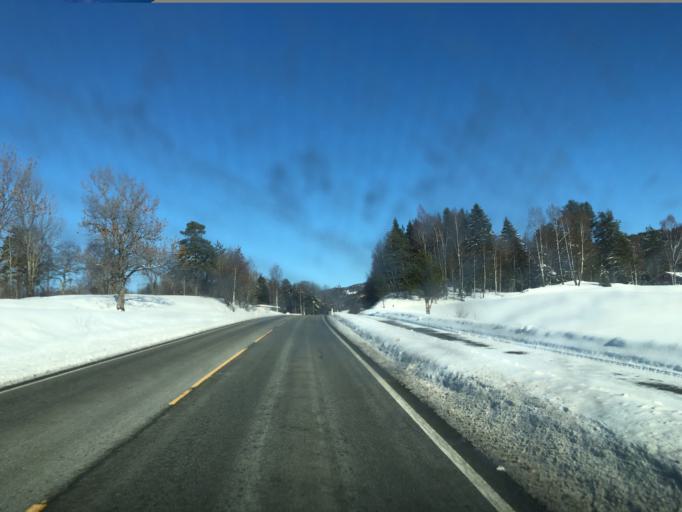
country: NO
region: Oppland
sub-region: Jevnaker
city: Jevnaker
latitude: 60.1781
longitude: 10.3470
